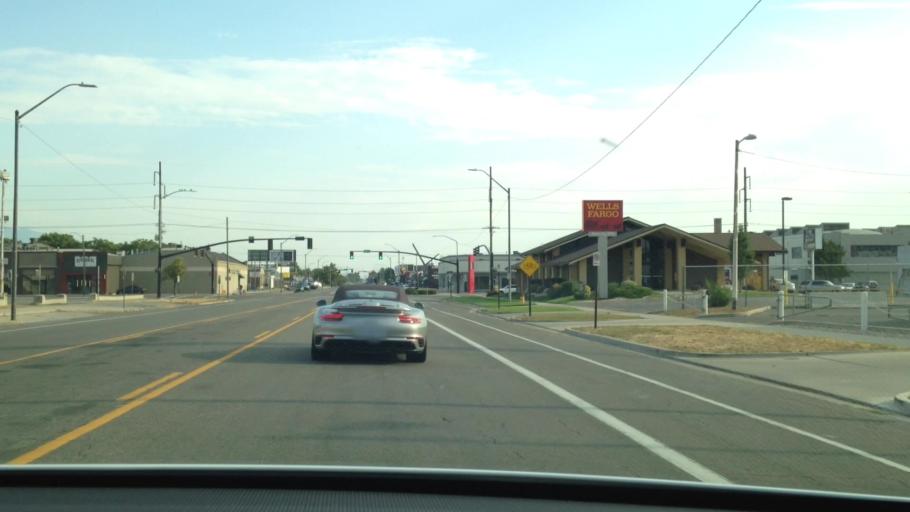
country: US
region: Utah
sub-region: Salt Lake County
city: Salt Lake City
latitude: 40.7532
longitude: -111.8910
